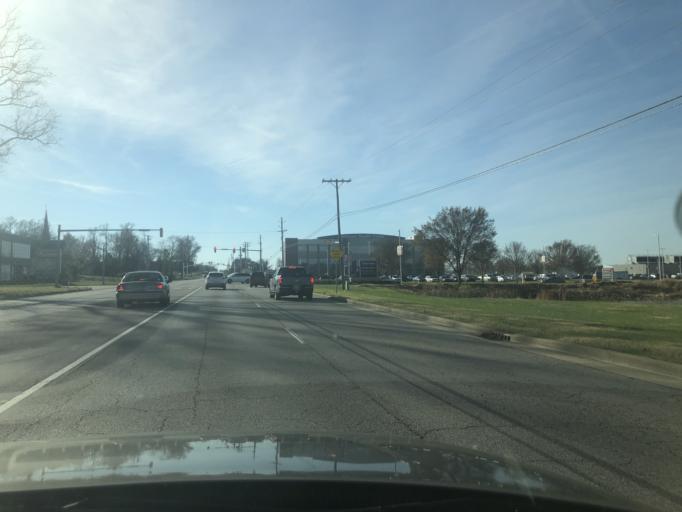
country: US
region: Indiana
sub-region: Warrick County
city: Newburgh
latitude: 37.9754
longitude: -87.4412
